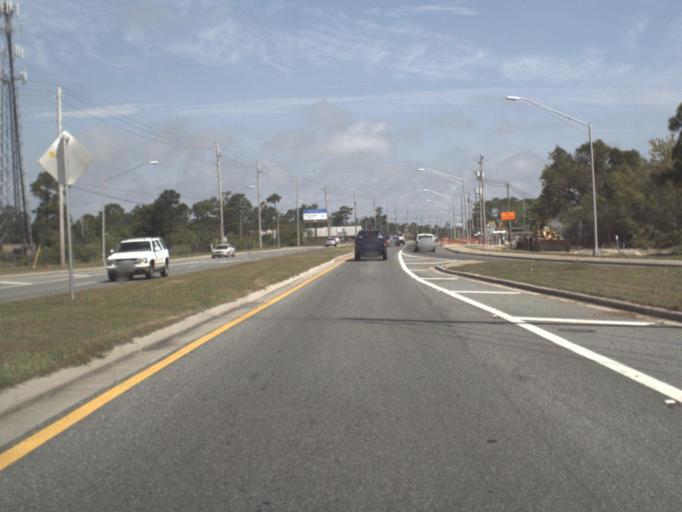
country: US
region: Florida
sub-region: Santa Rosa County
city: Navarre
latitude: 30.4037
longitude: -86.8712
